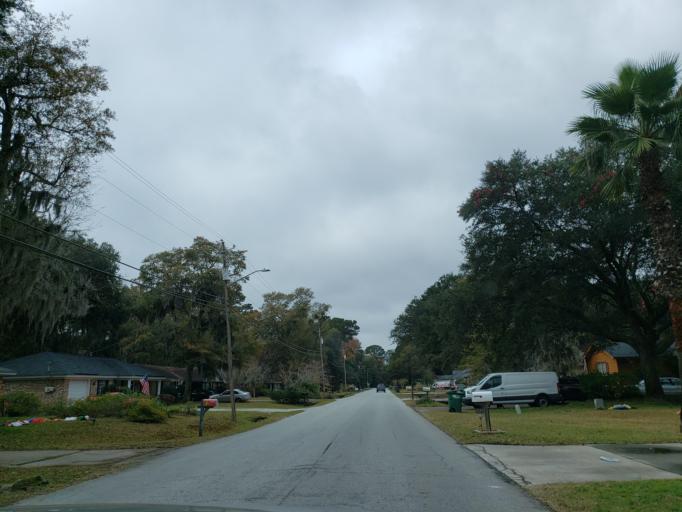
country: US
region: Georgia
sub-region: Chatham County
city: Wilmington Island
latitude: 32.0102
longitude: -80.9700
